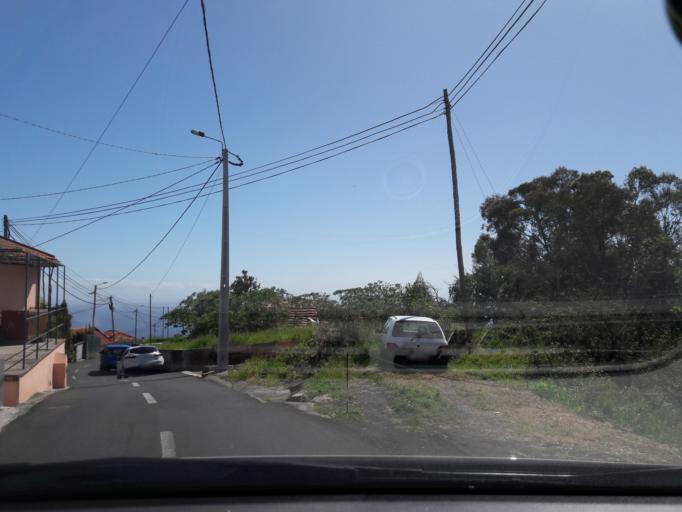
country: PT
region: Madeira
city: Camara de Lobos
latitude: 32.6733
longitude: -16.9544
